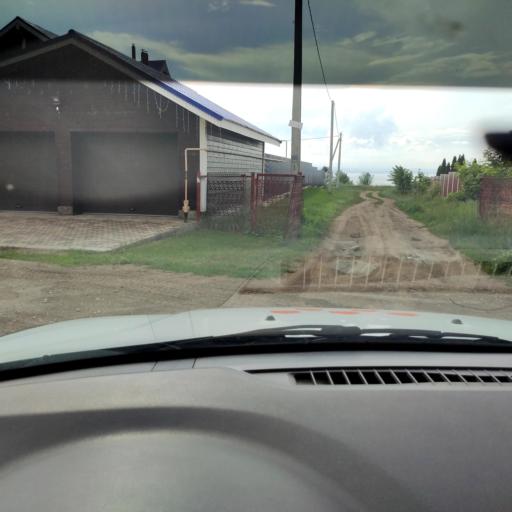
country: RU
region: Samara
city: Podstepki
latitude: 53.6103
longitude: 49.0311
